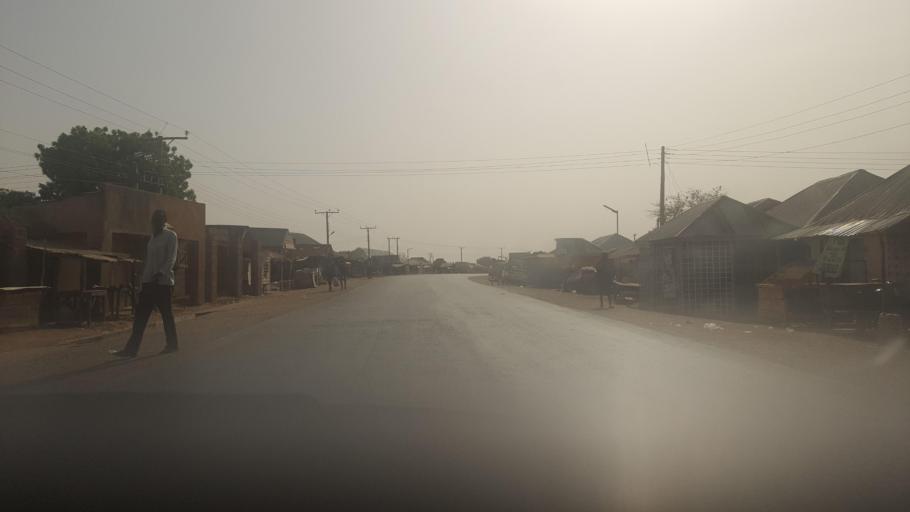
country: NG
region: Bauchi
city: Dindima
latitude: 10.2617
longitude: 9.9966
